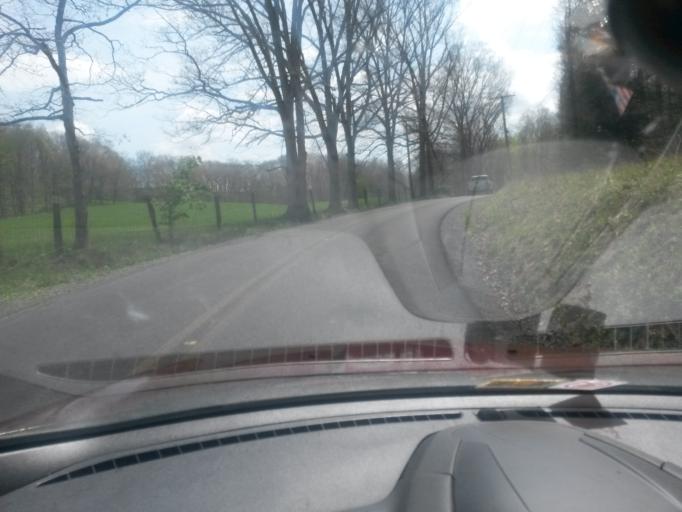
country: US
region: West Virginia
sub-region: Pocahontas County
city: Marlinton
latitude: 38.1109
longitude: -80.2229
